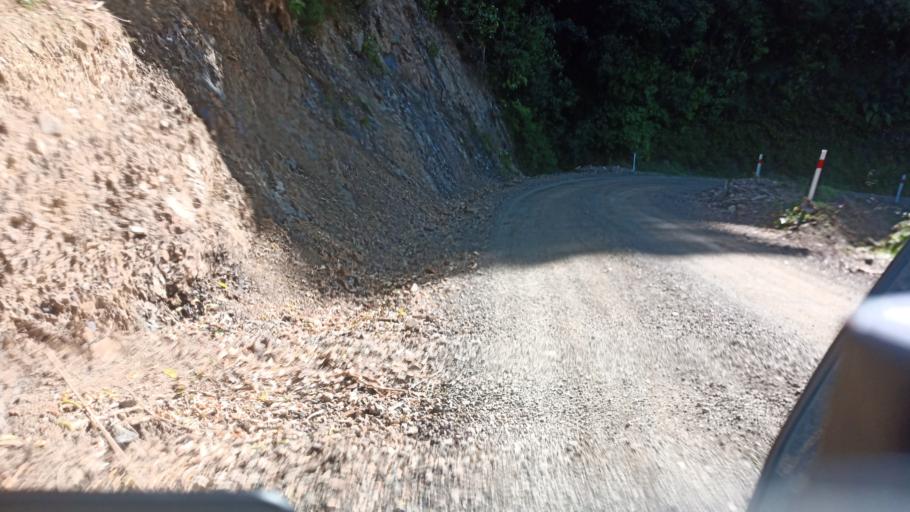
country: NZ
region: Bay of Plenty
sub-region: Opotiki District
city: Opotiki
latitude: -38.0618
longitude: 177.4639
